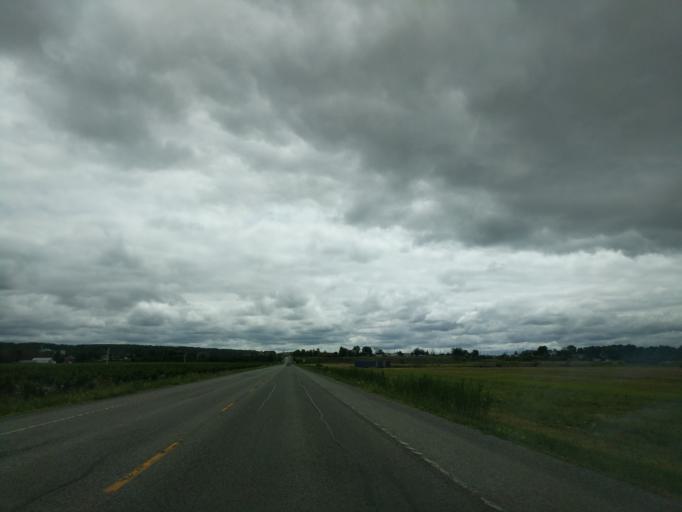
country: CA
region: Ontario
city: Thorold
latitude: 43.1705
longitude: -79.1686
